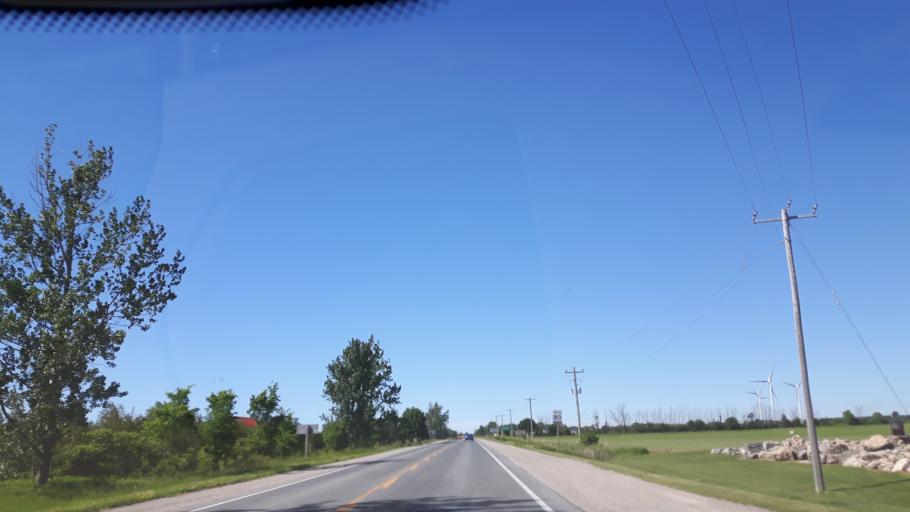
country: CA
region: Ontario
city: Bluewater
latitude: 43.4154
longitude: -81.7058
